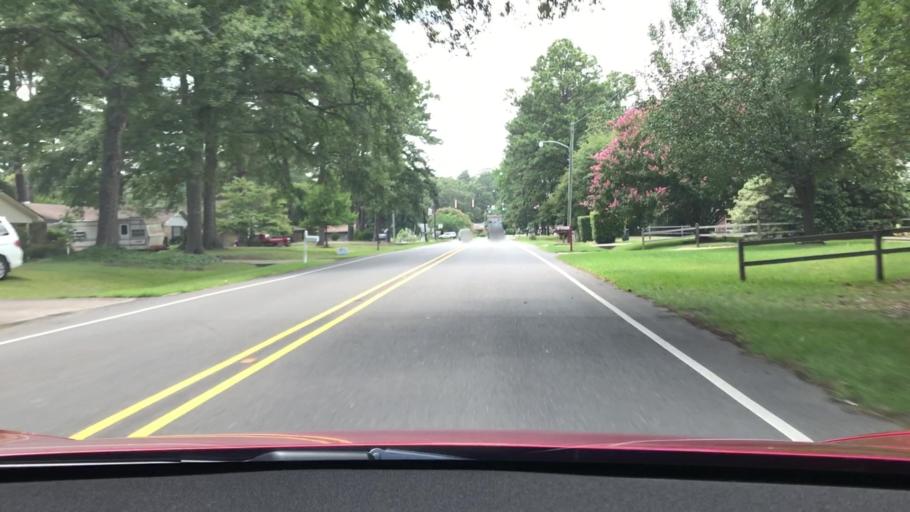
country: US
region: Louisiana
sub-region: De Soto Parish
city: Stonewall
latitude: 32.3909
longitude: -93.7946
